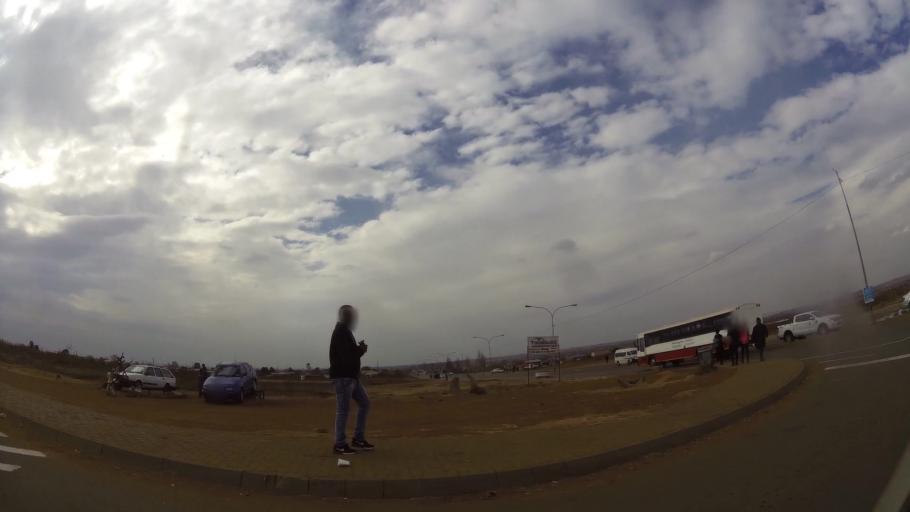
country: ZA
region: Gauteng
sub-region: Ekurhuleni Metropolitan Municipality
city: Germiston
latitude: -26.3961
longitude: 28.1578
